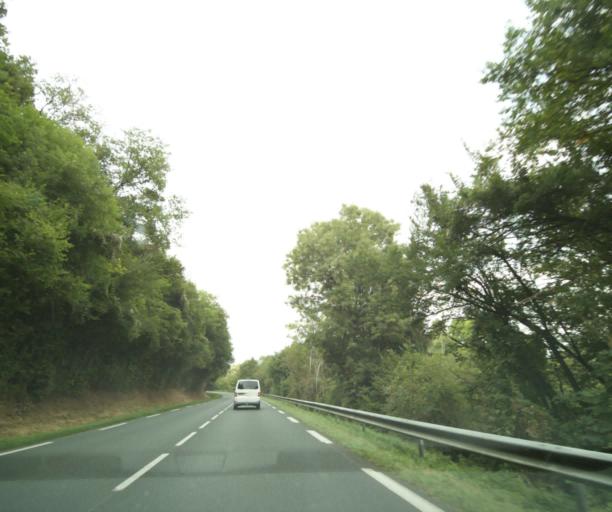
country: FR
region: Centre
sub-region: Departement de l'Indre
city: Clion
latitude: 46.9572
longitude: 1.2154
